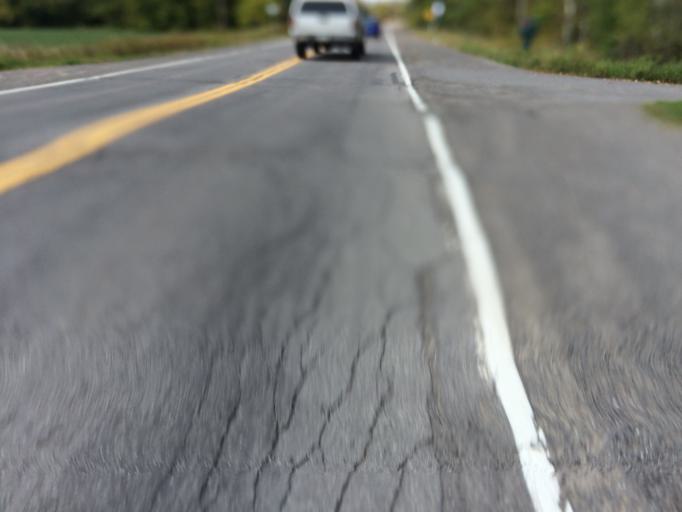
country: CA
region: Ontario
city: Bells Corners
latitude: 45.2080
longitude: -75.6589
